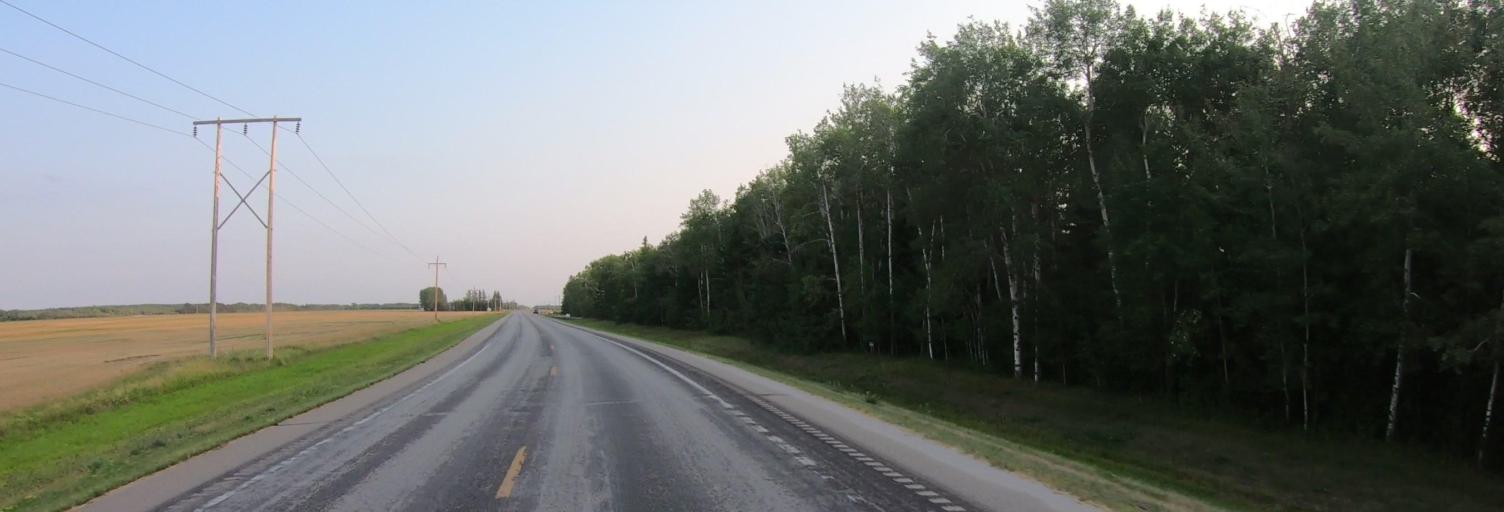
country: US
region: Minnesota
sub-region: Roseau County
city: Warroad
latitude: 48.8659
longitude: -95.3306
